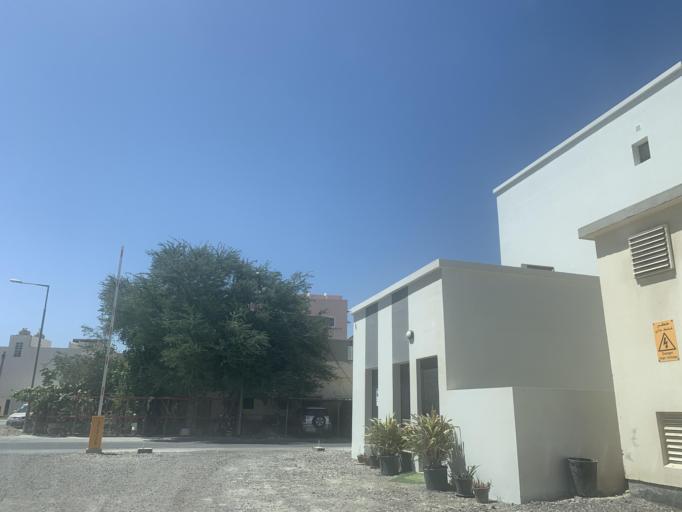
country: BH
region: Manama
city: Jidd Hafs
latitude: 26.2179
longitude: 50.4507
